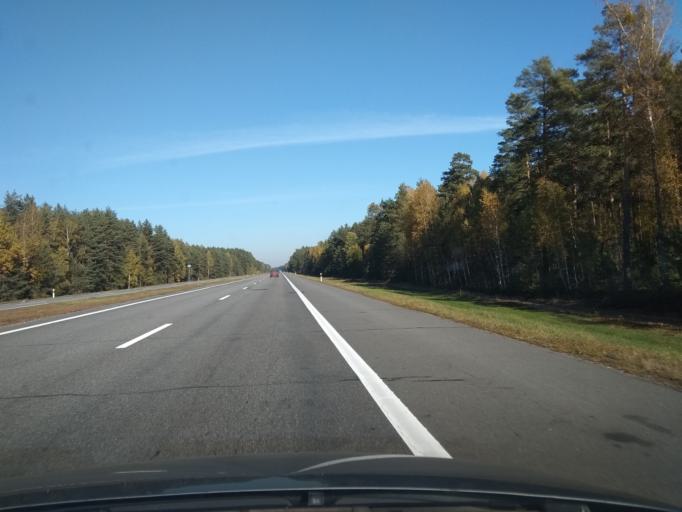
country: BY
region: Brest
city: Baranovichi
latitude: 52.9552
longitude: 25.7218
